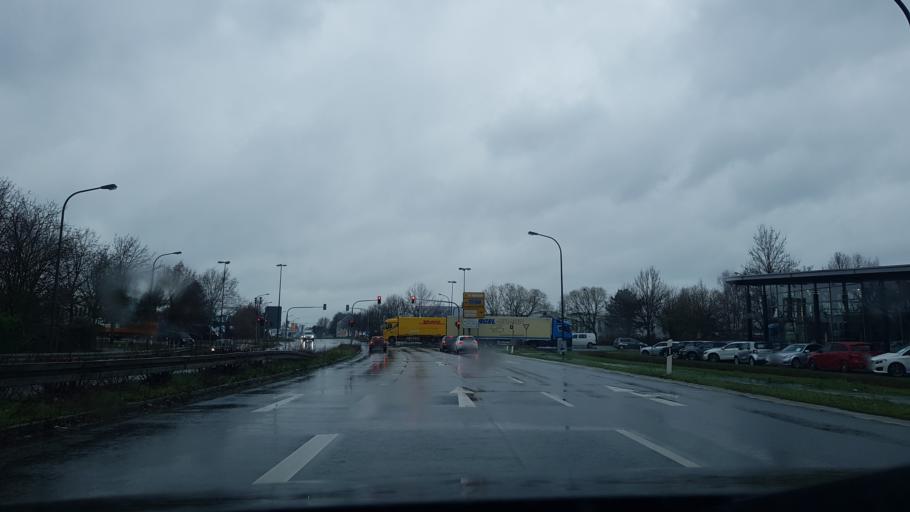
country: DE
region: North Rhine-Westphalia
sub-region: Regierungsbezirk Dusseldorf
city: Langenfeld
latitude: 51.1185
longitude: 6.9299
